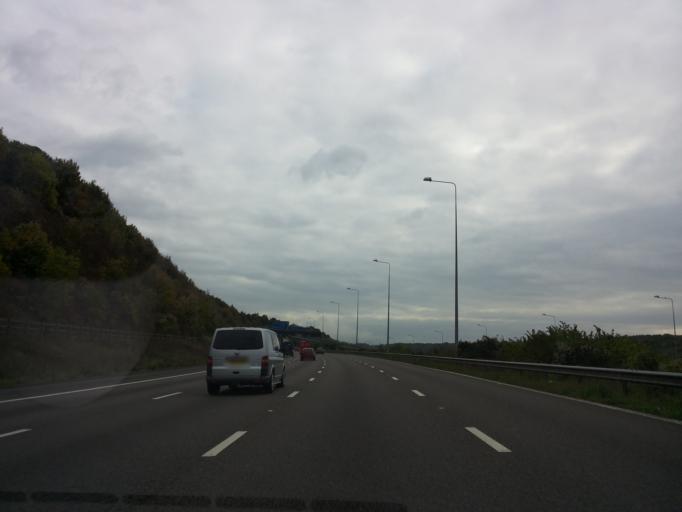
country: GB
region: England
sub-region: Medway
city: Rochester
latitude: 51.3604
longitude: 0.4913
